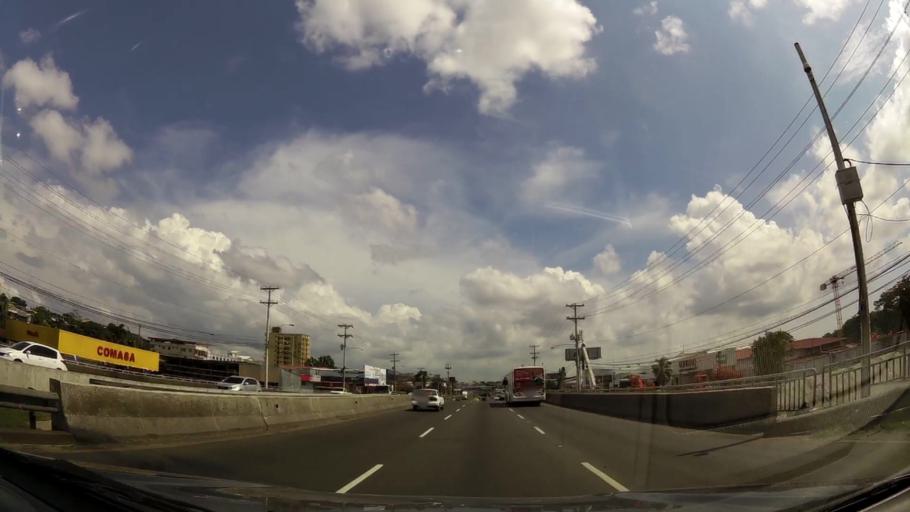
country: PA
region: Panama
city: San Miguelito
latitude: 9.0351
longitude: -79.4846
